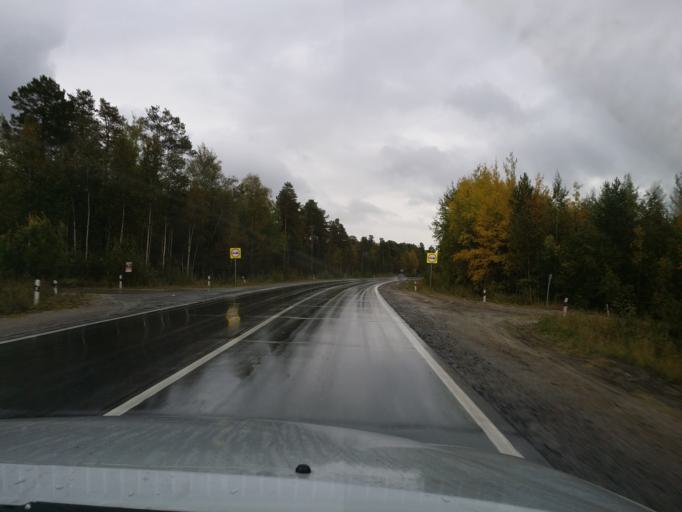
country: RU
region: Khanty-Mansiyskiy Avtonomnyy Okrug
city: Megion
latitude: 61.1253
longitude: 75.8244
